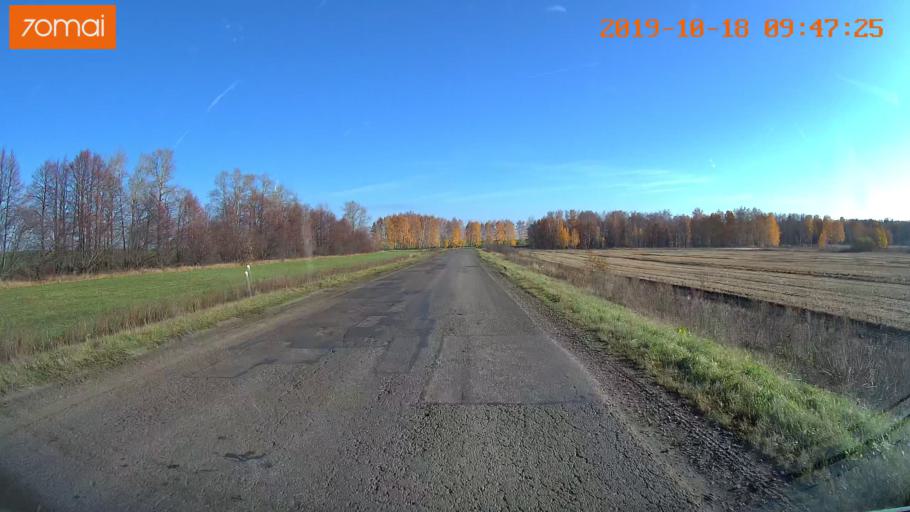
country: RU
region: Tula
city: Kazachka
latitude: 53.3187
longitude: 38.2311
